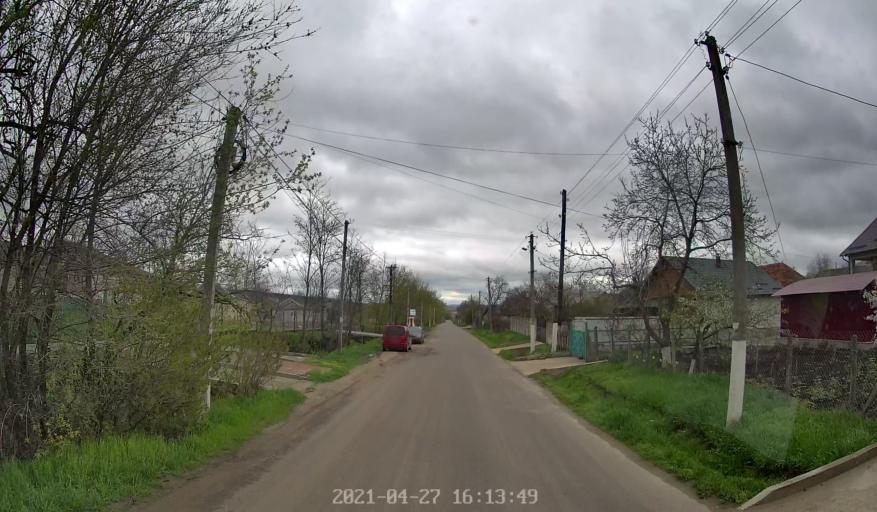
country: MD
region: Chisinau
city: Singera
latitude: 47.0066
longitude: 29.0137
